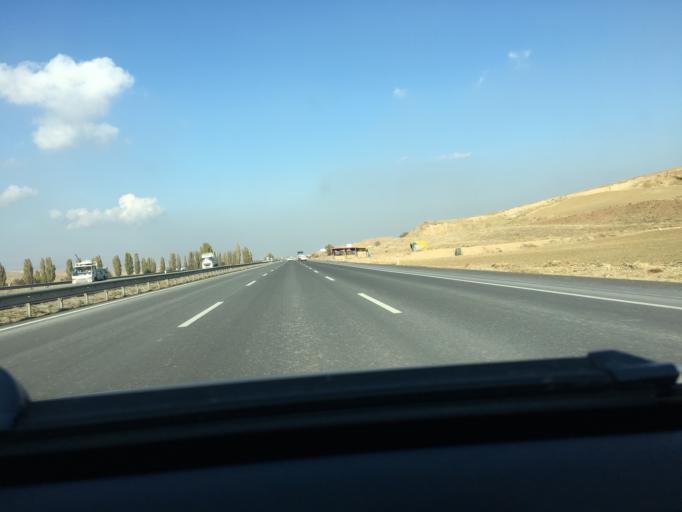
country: TR
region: Ankara
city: Polatli
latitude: 39.6301
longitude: 32.1961
